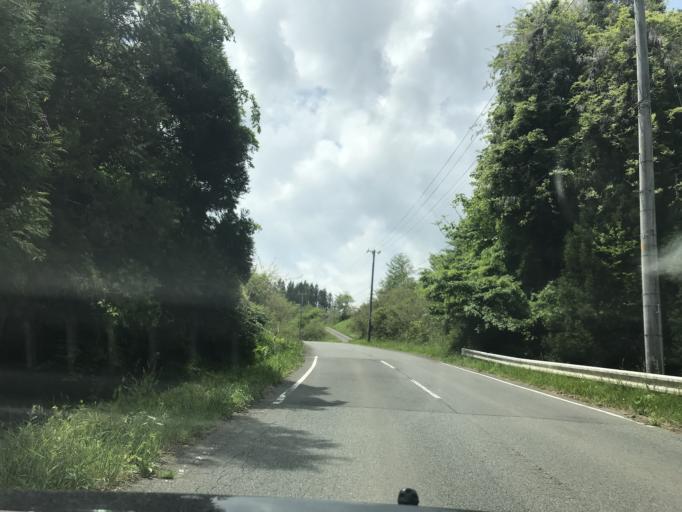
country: JP
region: Miyagi
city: Furukawa
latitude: 38.7352
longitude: 140.9272
